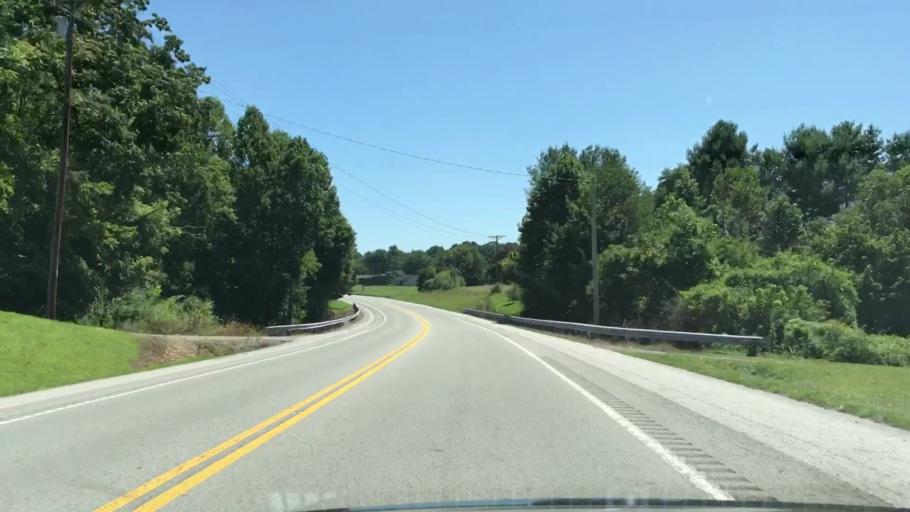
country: US
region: Tennessee
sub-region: Jackson County
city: Gainesboro
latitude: 36.2848
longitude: -85.6294
